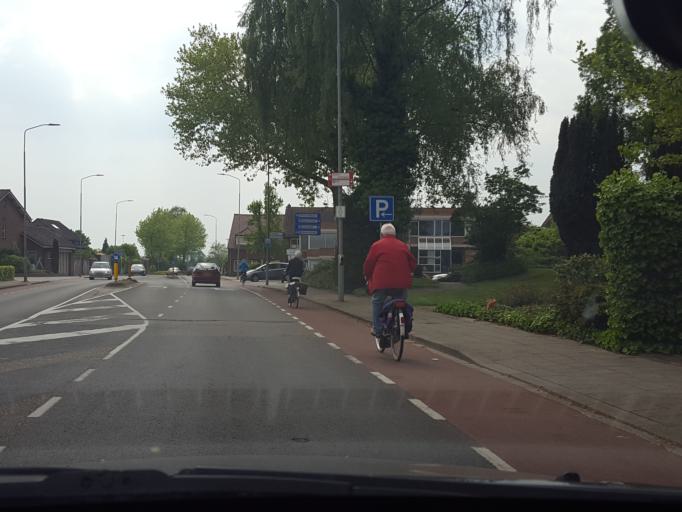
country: NL
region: Gelderland
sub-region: Gemeente Winterswijk
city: Winterswijk
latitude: 51.9685
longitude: 6.7210
